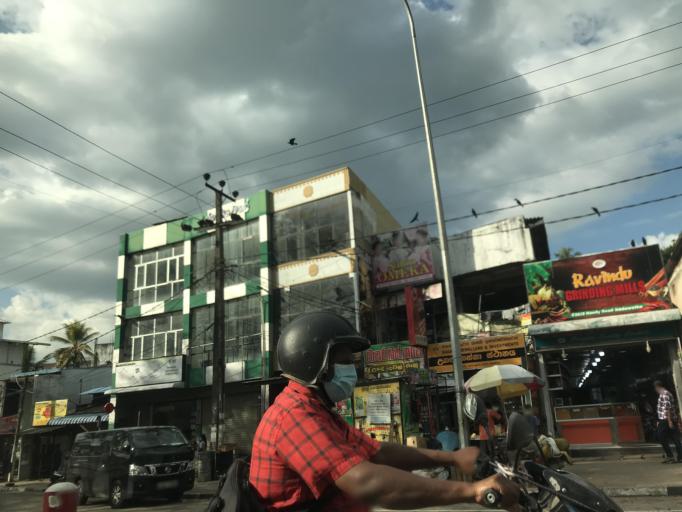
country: LK
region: Western
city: Kelaniya
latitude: 7.0020
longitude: 79.9515
